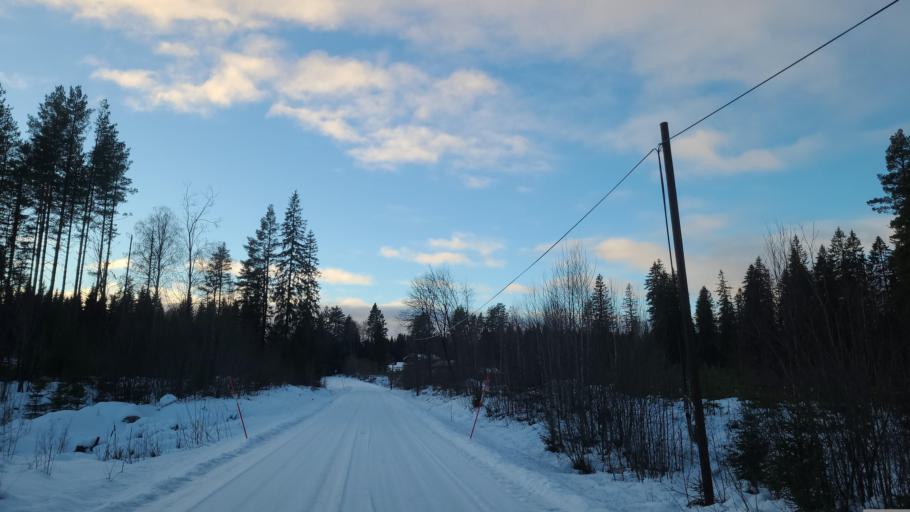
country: SE
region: Gaevleborg
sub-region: Bollnas Kommun
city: Kilafors
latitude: 61.3843
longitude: 16.6900
